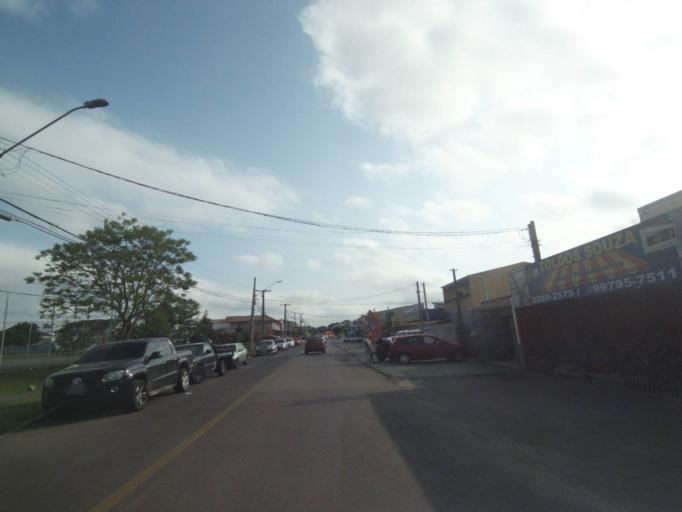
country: BR
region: Parana
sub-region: Sao Jose Dos Pinhais
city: Sao Jose dos Pinhais
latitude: -25.5433
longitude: -49.2578
